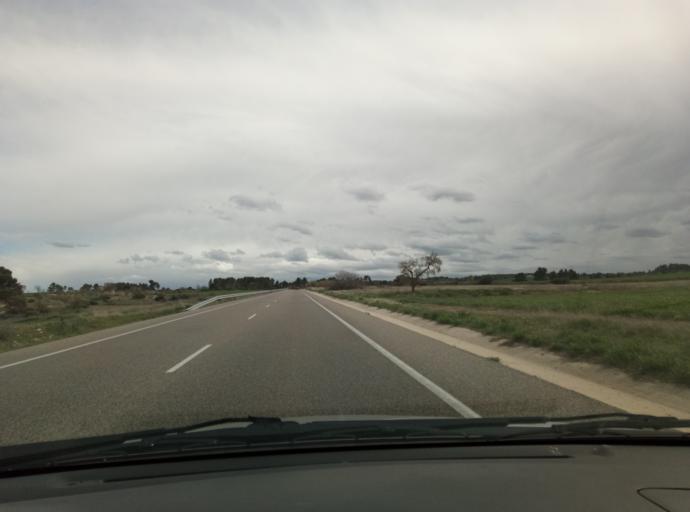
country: ES
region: Catalonia
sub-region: Provincia de Lleida
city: Ciutadilla
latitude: 41.5435
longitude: 1.1457
